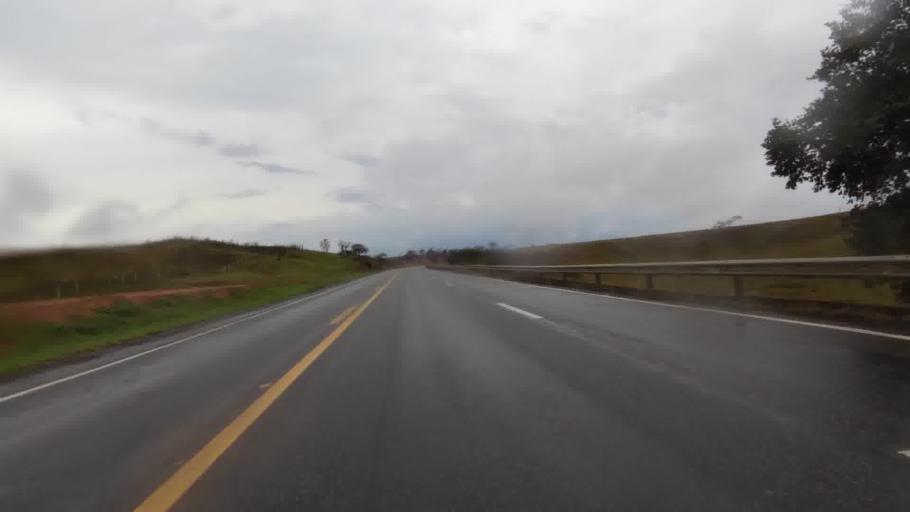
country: BR
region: Rio de Janeiro
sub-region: Campos Dos Goytacazes
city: Campos
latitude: -21.5103
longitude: -41.3355
